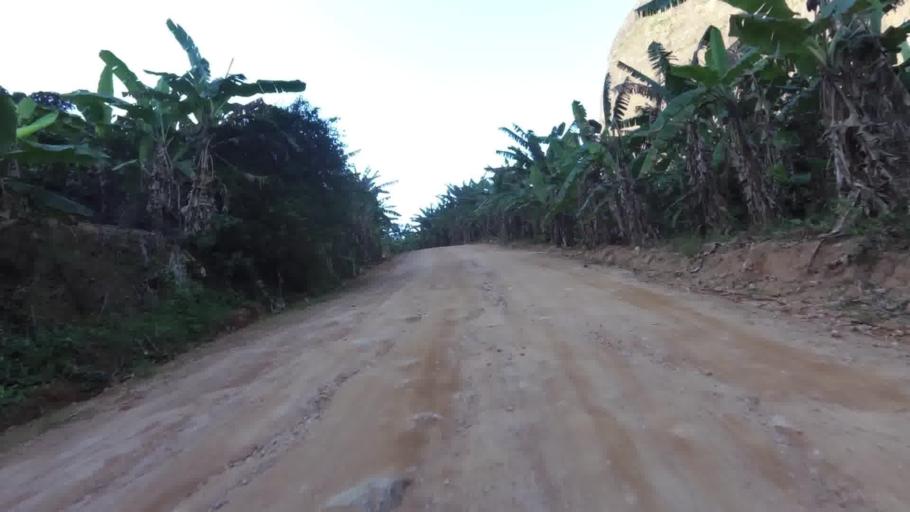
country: BR
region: Espirito Santo
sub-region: Alfredo Chaves
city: Alfredo Chaves
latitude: -20.5607
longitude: -40.6923
